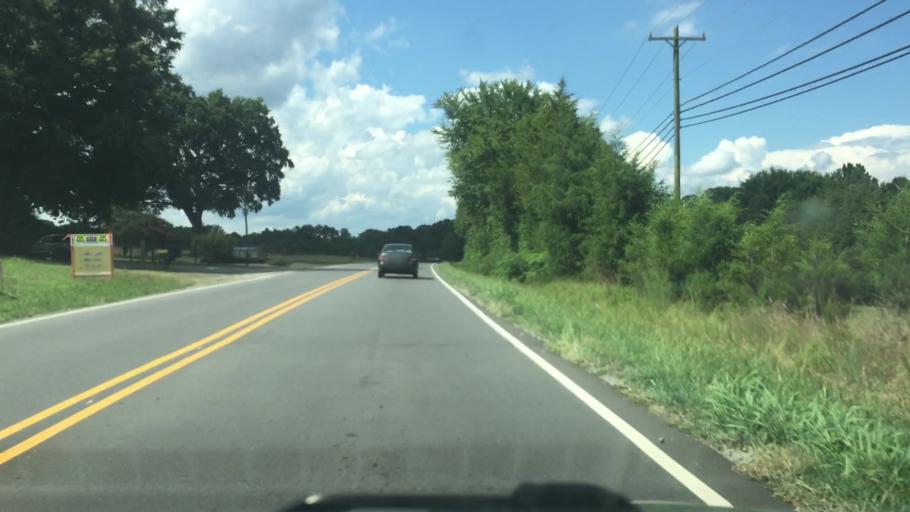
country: US
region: North Carolina
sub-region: Rowan County
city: Enochville
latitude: 35.4537
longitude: -80.7318
